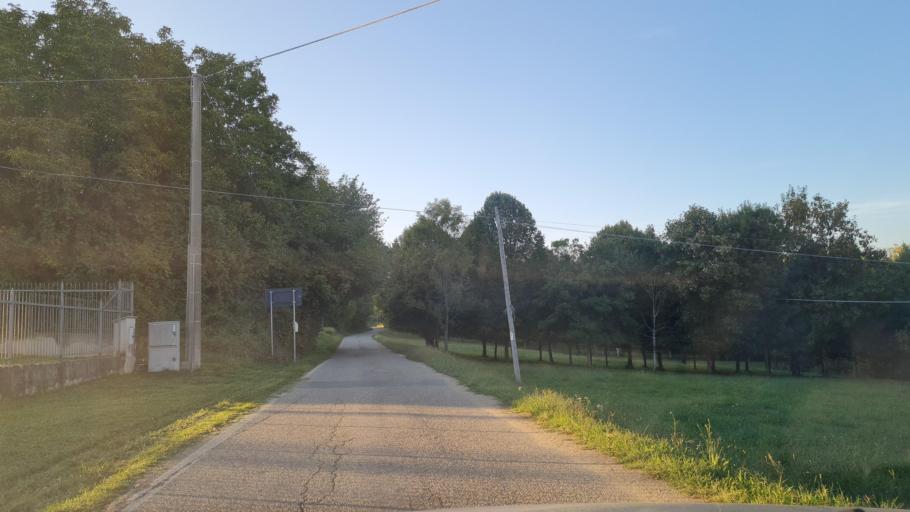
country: IT
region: Piedmont
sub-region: Provincia di Biella
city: Zubiena
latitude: 45.4865
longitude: 8.0080
